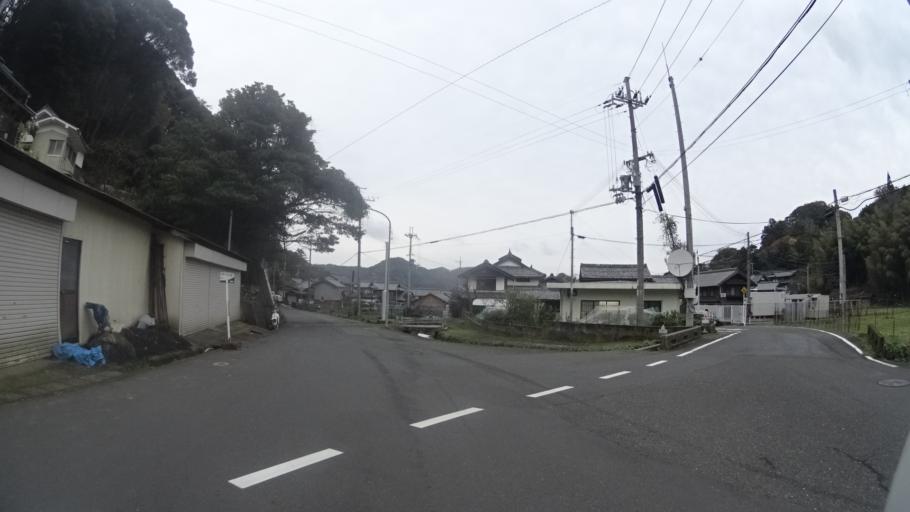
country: JP
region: Kyoto
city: Maizuru
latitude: 35.5654
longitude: 135.4539
